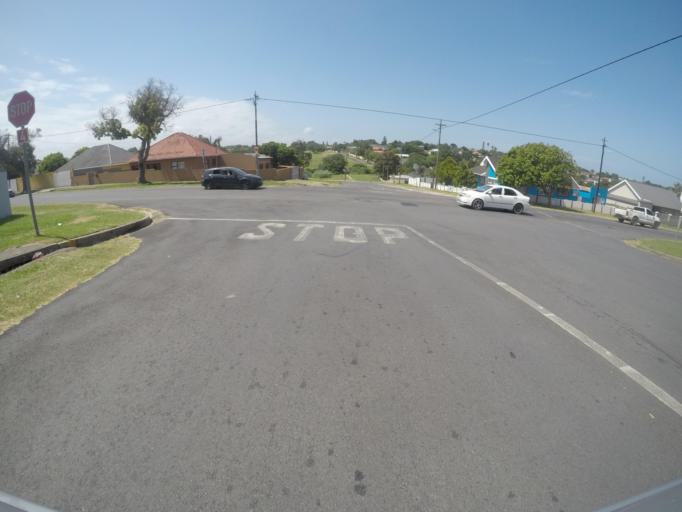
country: ZA
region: Eastern Cape
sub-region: Buffalo City Metropolitan Municipality
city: East London
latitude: -32.9782
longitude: 27.8758
